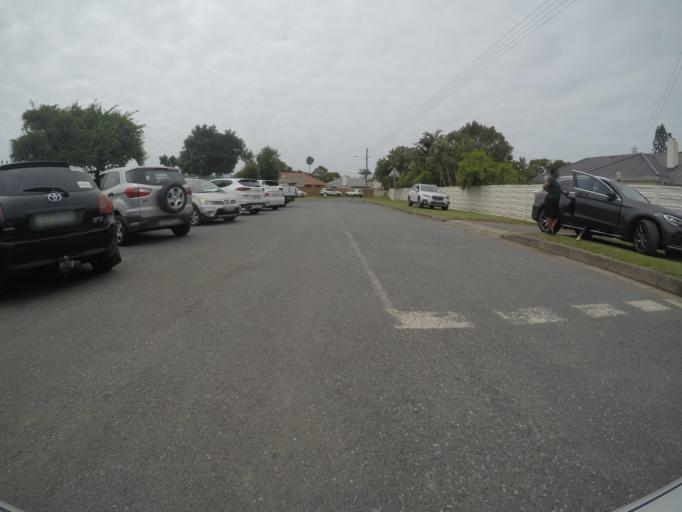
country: ZA
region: Eastern Cape
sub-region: Buffalo City Metropolitan Municipality
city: East London
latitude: -32.9704
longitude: 27.9368
